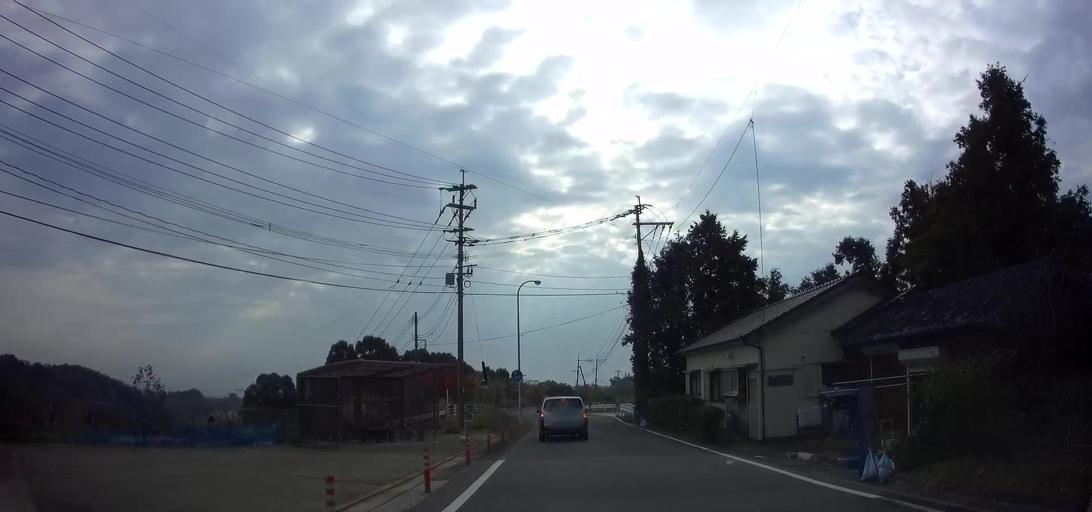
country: JP
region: Nagasaki
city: Shimabara
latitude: 32.6826
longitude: 130.2747
